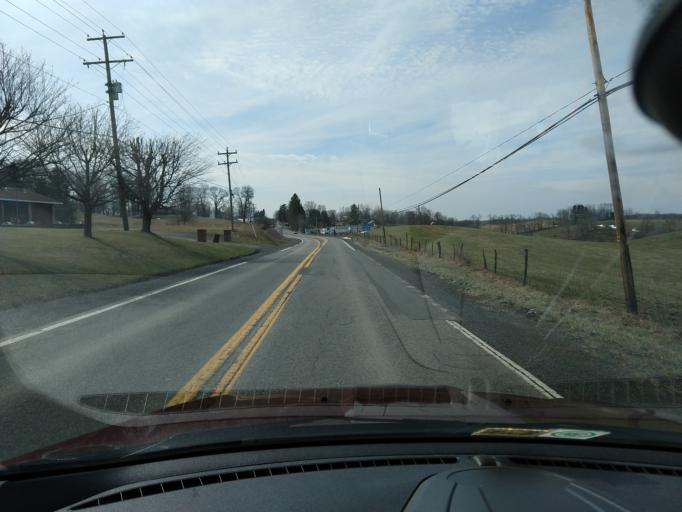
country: US
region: West Virginia
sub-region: Greenbrier County
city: Lewisburg
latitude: 37.8591
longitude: -80.4114
